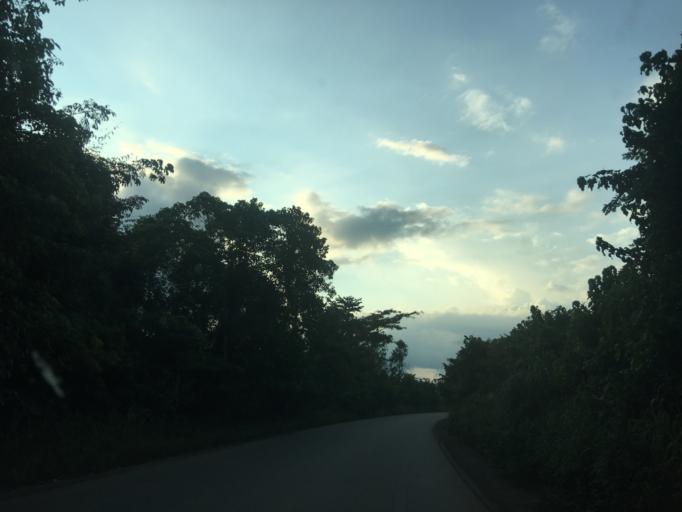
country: GH
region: Western
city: Bibiani
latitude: 6.6345
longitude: -2.4238
